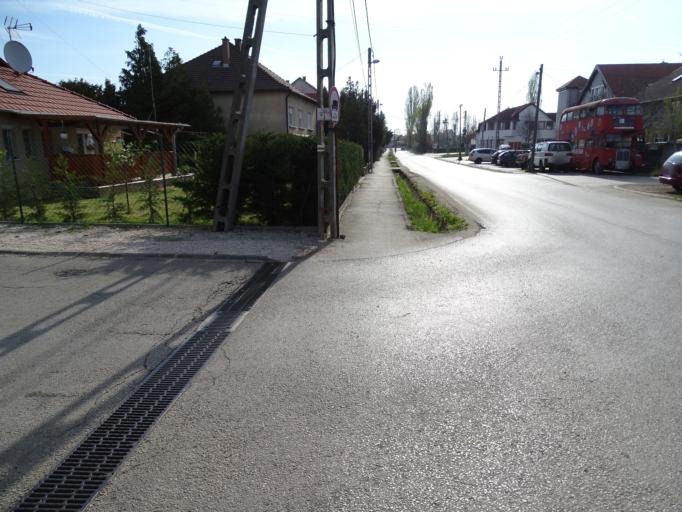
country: HU
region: Pest
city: Szentendre
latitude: 47.6625
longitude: 19.0647
